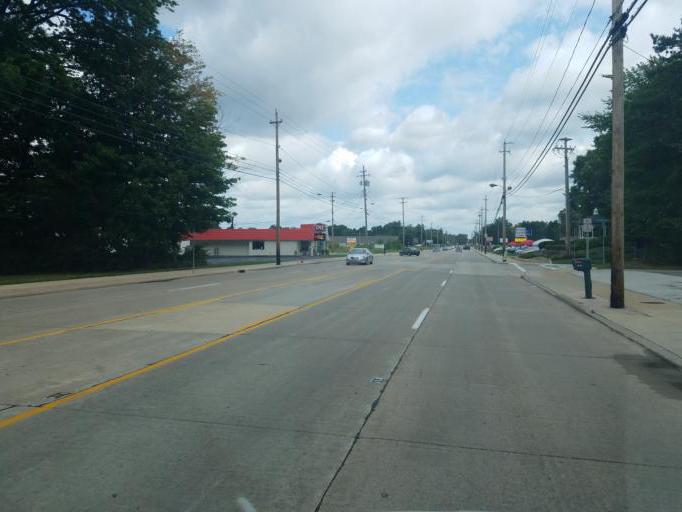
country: US
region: Ohio
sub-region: Lake County
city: Painesville
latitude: 41.6892
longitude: -81.2886
